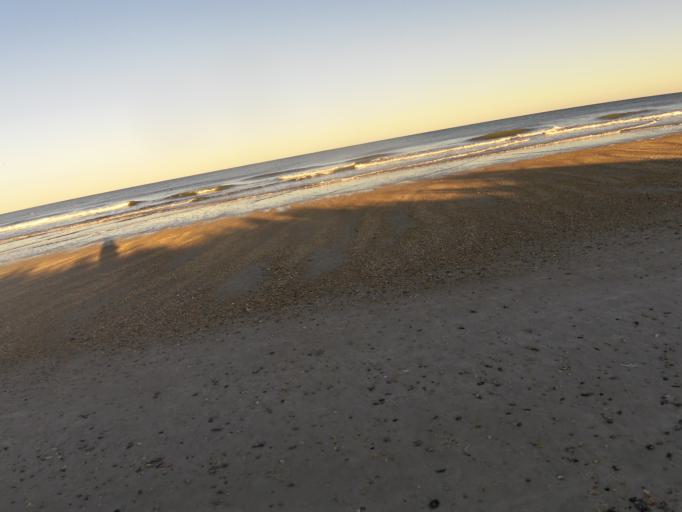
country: US
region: Florida
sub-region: Duval County
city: Atlantic Beach
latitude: 30.4631
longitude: -81.4117
